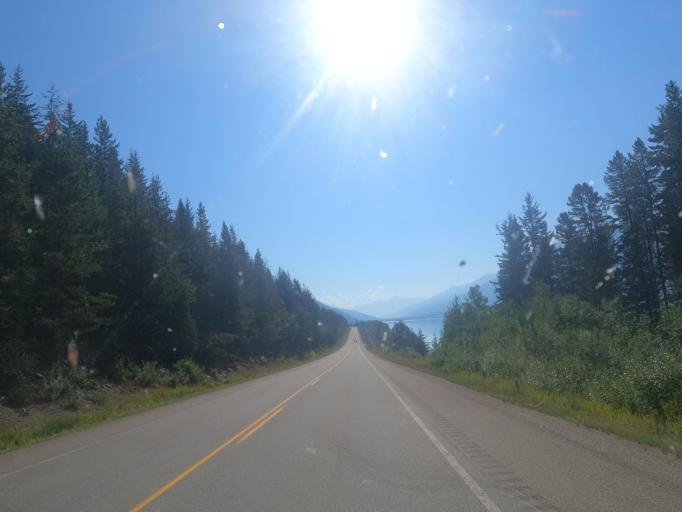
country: CA
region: Alberta
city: Jasper Park Lodge
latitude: 52.9612
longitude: -118.9084
